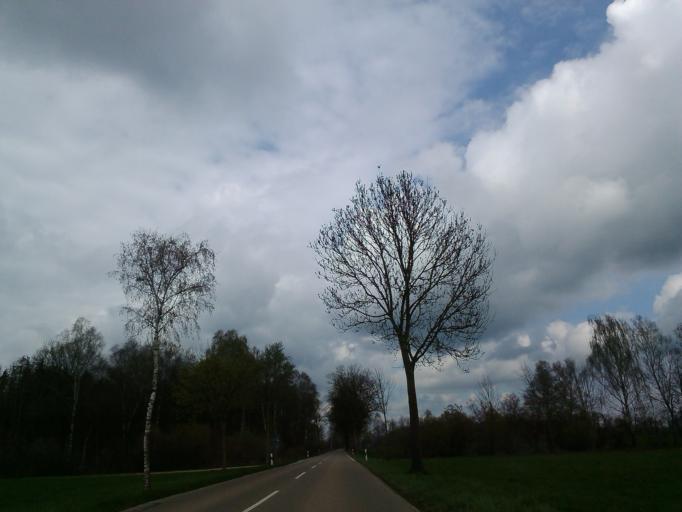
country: DE
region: Baden-Wuerttemberg
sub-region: Tuebingen Region
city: Langenau
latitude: 48.4742
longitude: 10.1545
